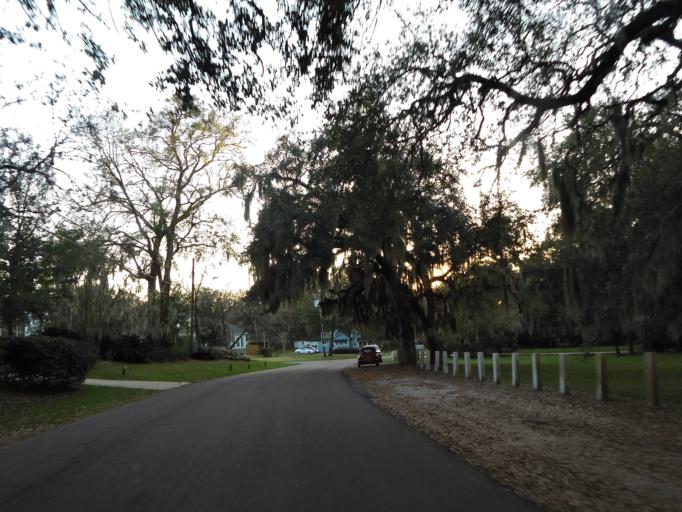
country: US
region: Florida
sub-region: Duval County
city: Jacksonville
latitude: 30.2731
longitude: -81.7070
